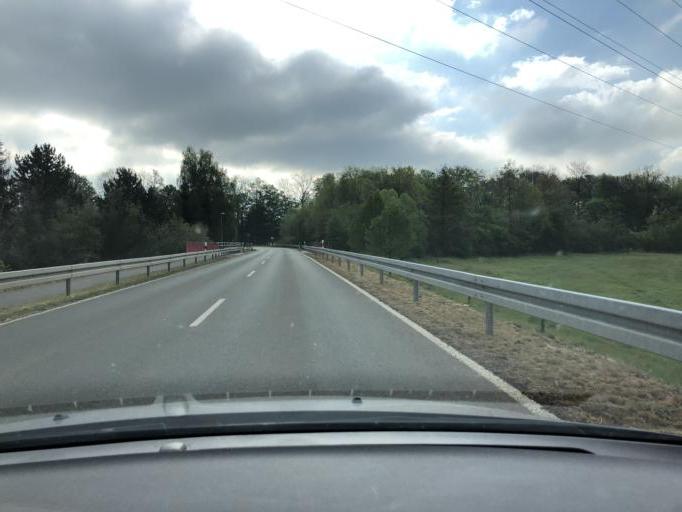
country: DE
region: Thuringia
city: Haselbach
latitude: 51.0531
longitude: 12.4448
